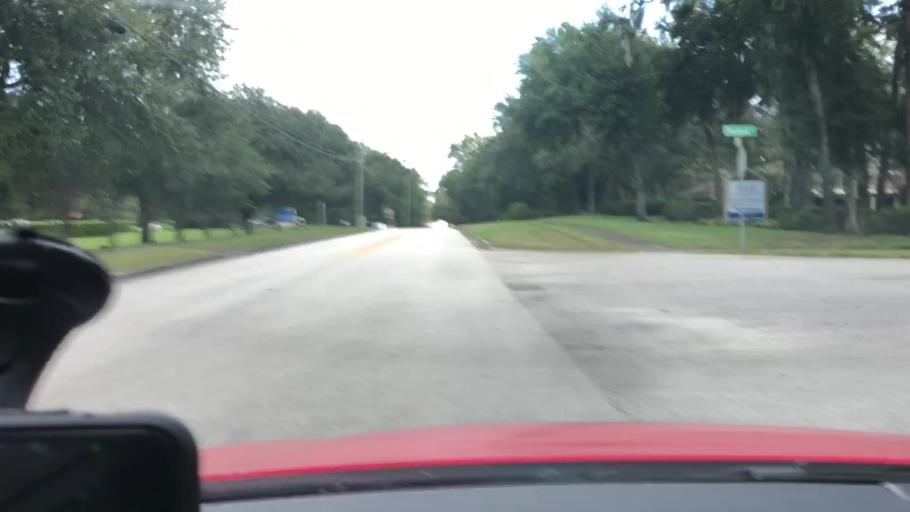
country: US
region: Florida
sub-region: Volusia County
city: North DeLand
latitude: 29.0448
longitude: -81.3164
